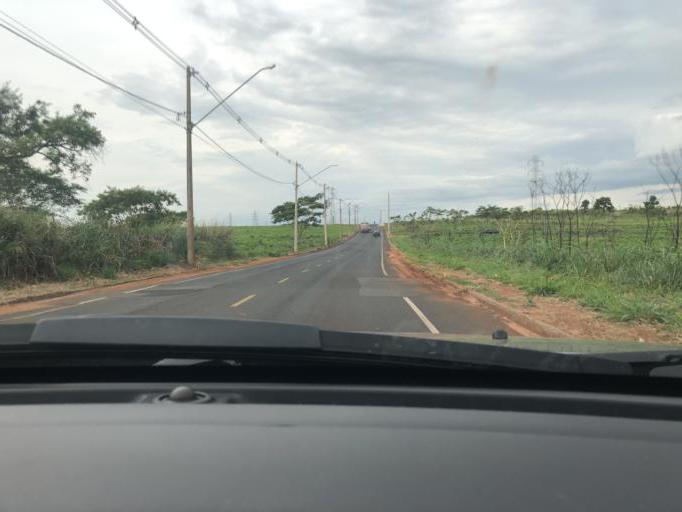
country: BR
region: Sao Paulo
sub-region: Sao Jose Do Rio Preto
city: Sao Jose do Rio Preto
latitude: -20.8321
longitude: -49.4254
